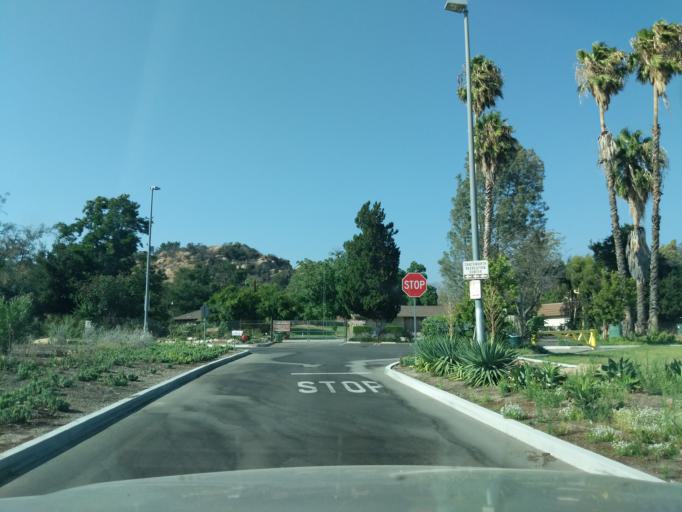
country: US
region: California
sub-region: Los Angeles County
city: Chatsworth
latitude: 34.2592
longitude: -118.6153
